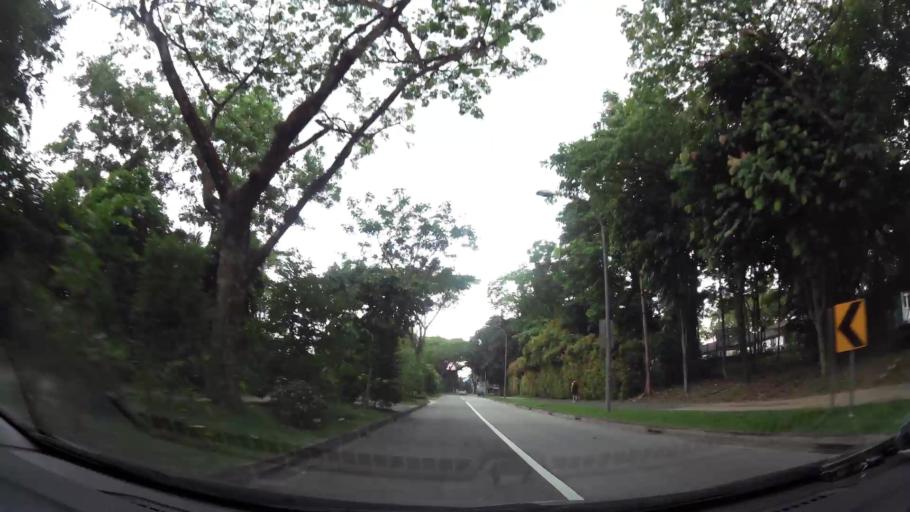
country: MY
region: Johor
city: Kampung Pasir Gudang Baru
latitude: 1.4551
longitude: 103.8338
